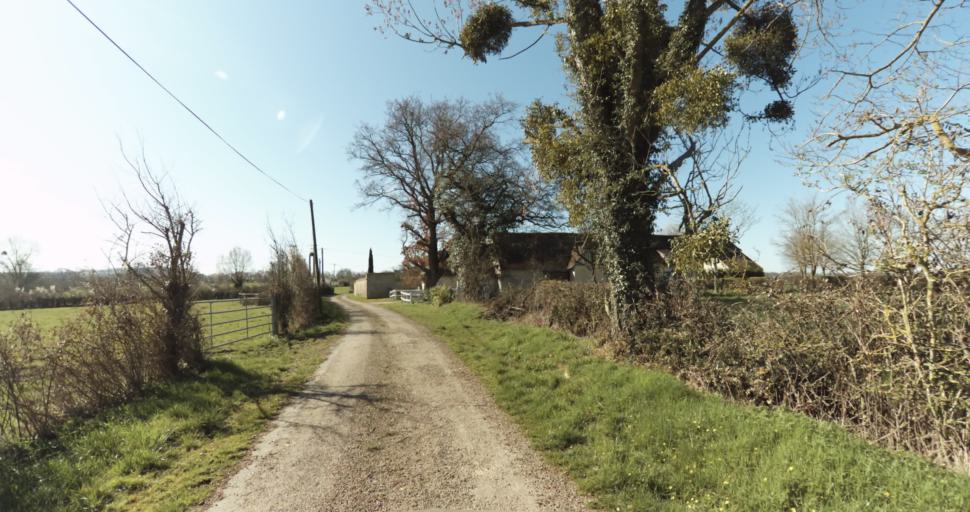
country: FR
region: Lower Normandy
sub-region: Departement de l'Orne
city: Trun
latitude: 48.9247
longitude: 0.0379
